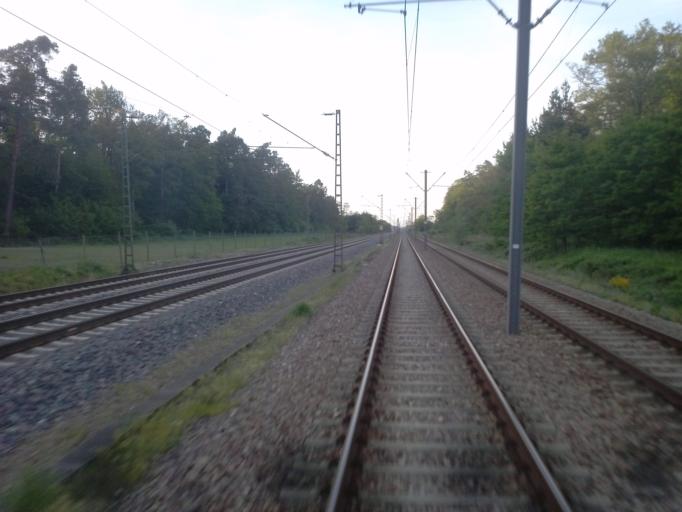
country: DE
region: Baden-Wuerttemberg
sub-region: Karlsruhe Region
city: Weingarten
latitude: 49.0919
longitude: 8.4720
